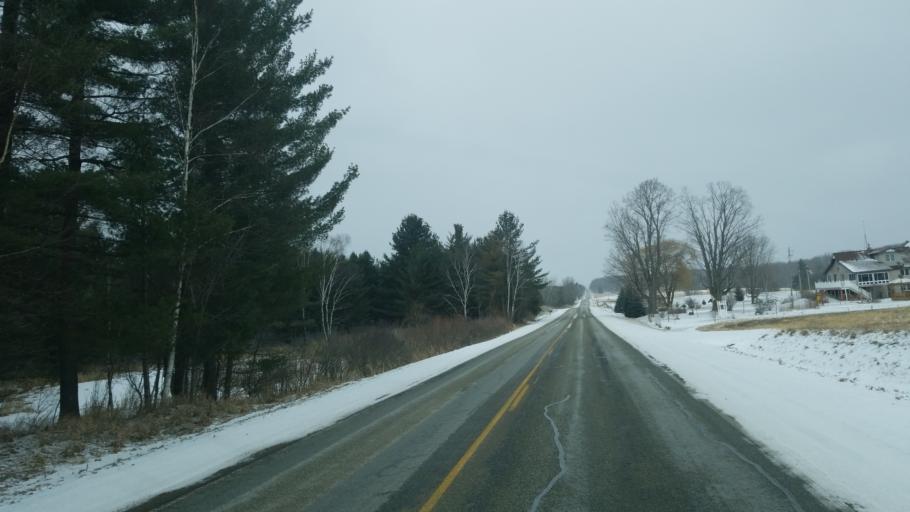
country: US
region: Michigan
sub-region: Osceola County
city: Evart
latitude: 43.9911
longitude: -85.2465
